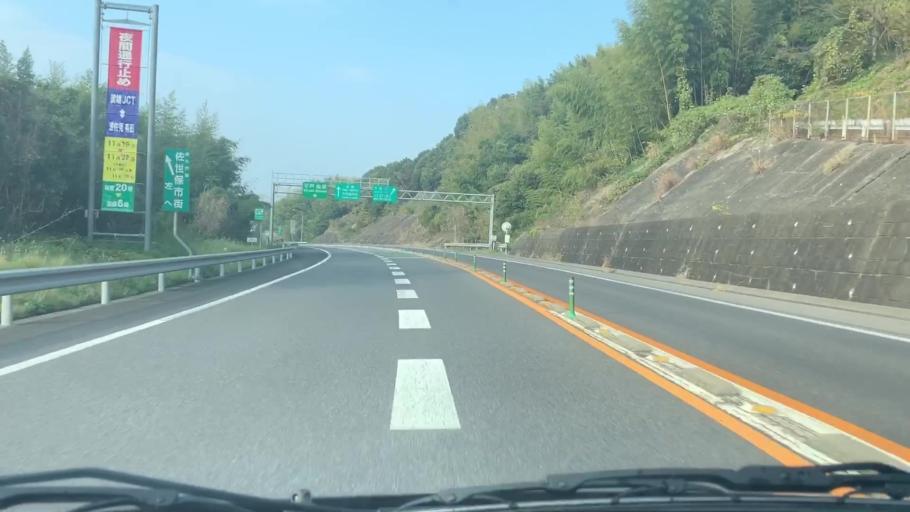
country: JP
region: Nagasaki
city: Sasebo
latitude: 33.1502
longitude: 129.7867
